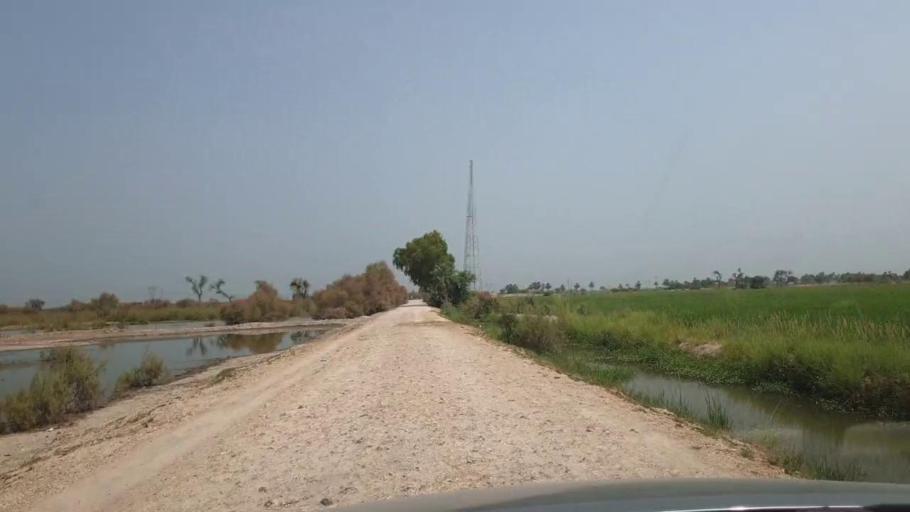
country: PK
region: Sindh
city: Madeji
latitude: 27.8018
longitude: 68.5317
